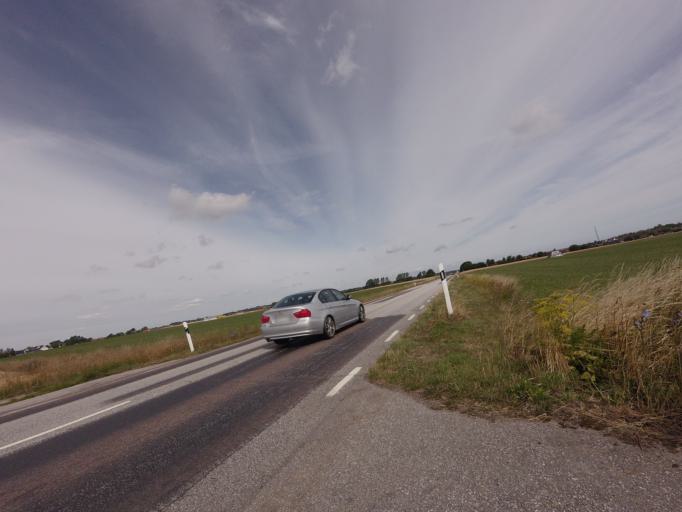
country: SE
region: Skane
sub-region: Simrishamns Kommun
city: Simrishamn
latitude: 55.5368
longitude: 14.3395
